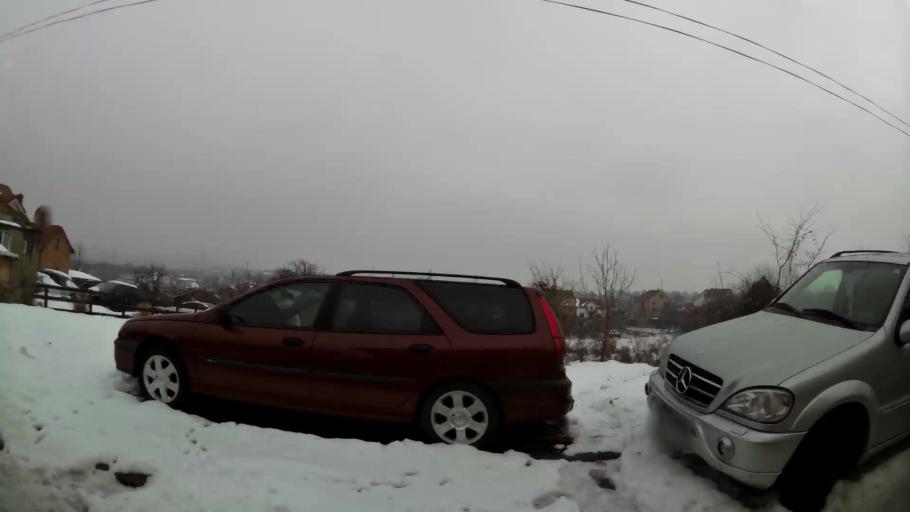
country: RS
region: Central Serbia
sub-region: Belgrade
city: Zvezdara
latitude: 44.7596
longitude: 20.5272
